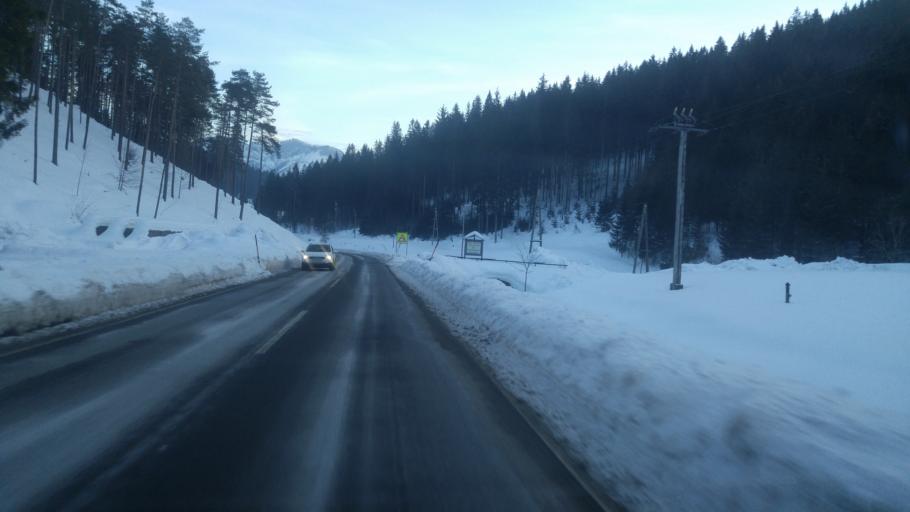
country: AT
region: Lower Austria
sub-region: Politischer Bezirk Wiener Neustadt
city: Rohr im Gebirge
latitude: 47.8723
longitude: 15.6978
